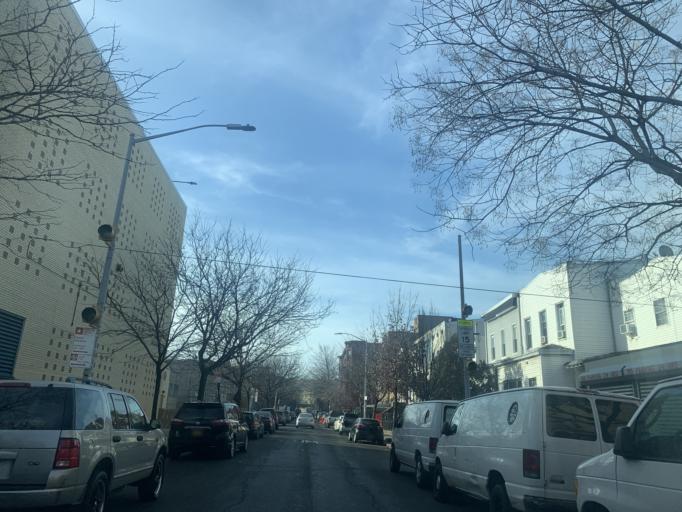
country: US
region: New York
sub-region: Kings County
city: East New York
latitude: 40.6913
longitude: -73.9180
